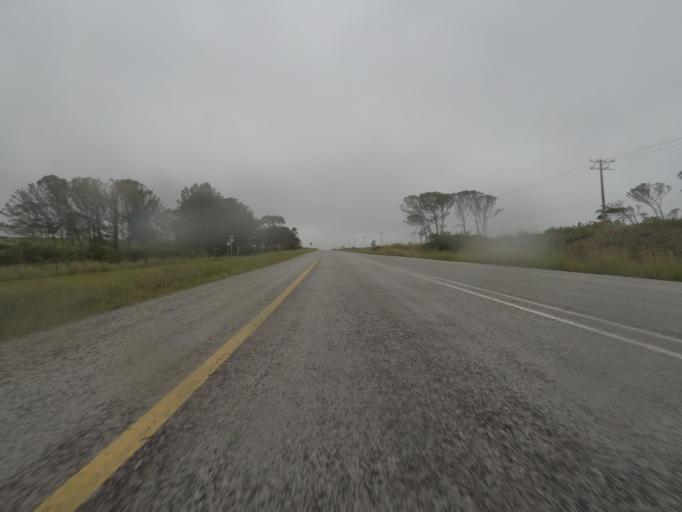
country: ZA
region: Eastern Cape
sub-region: Cacadu District Municipality
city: Grahamstown
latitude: -33.6439
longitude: 26.3556
